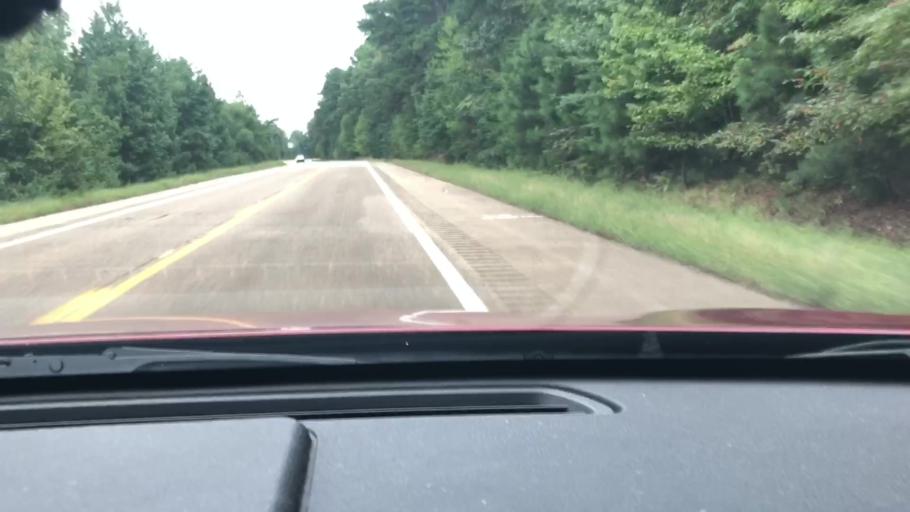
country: US
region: Arkansas
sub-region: Miller County
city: Texarkana
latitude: 33.4193
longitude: -93.8317
